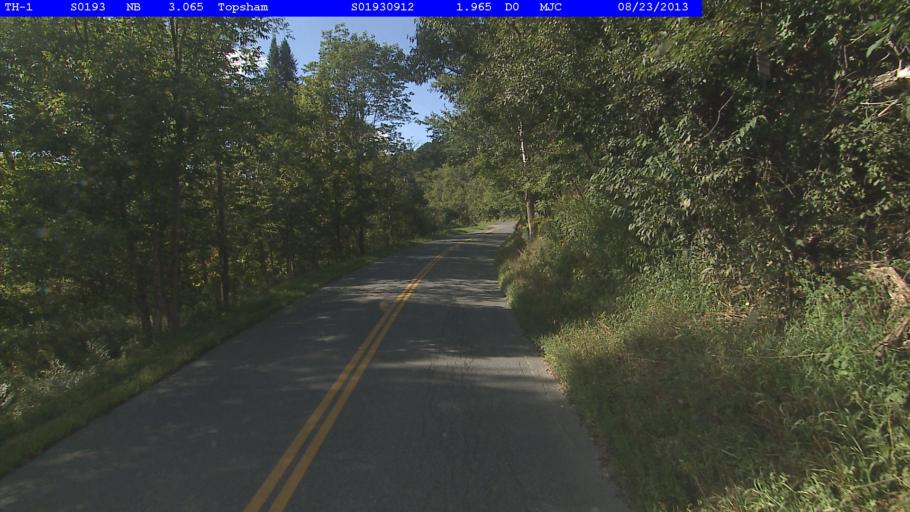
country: US
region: New Hampshire
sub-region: Grafton County
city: Haverhill
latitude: 44.0982
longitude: -72.2239
